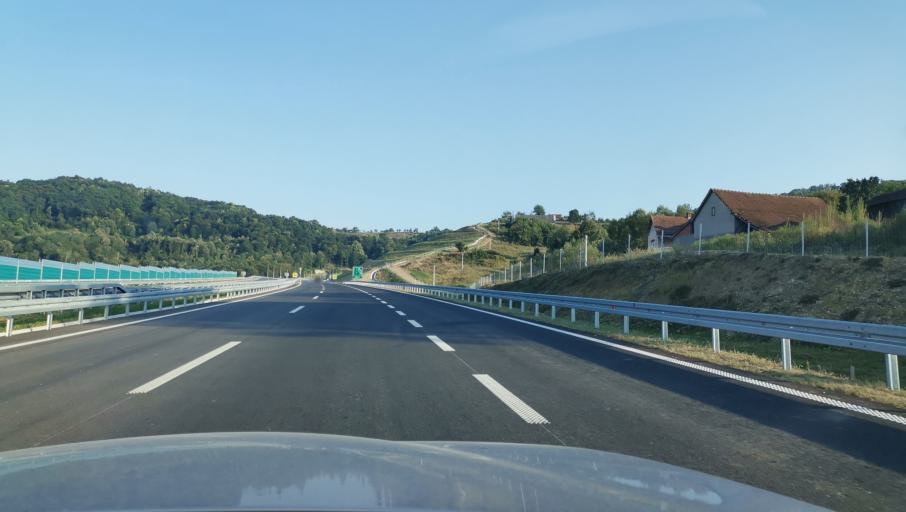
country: RS
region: Central Serbia
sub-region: Kolubarski Okrug
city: Ljig
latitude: 44.2172
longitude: 20.2578
